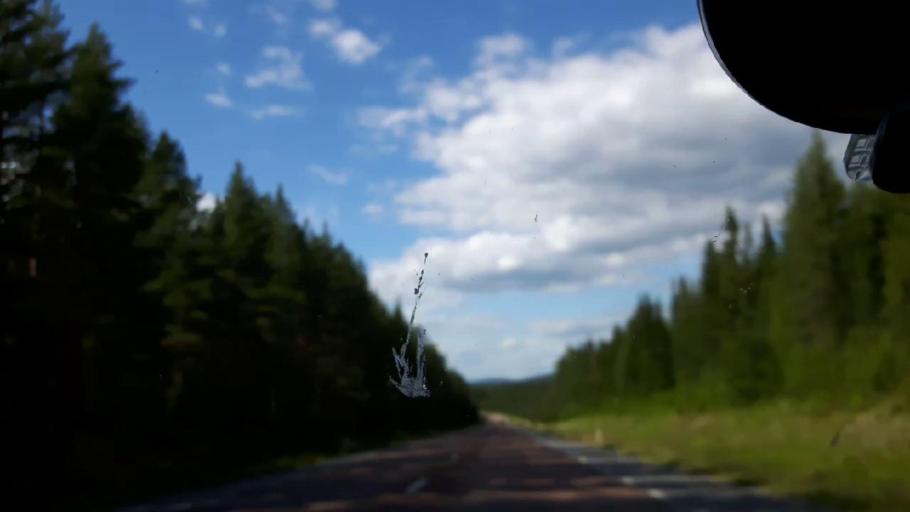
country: SE
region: Jaemtland
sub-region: Braecke Kommun
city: Braecke
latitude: 62.8093
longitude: 15.3661
